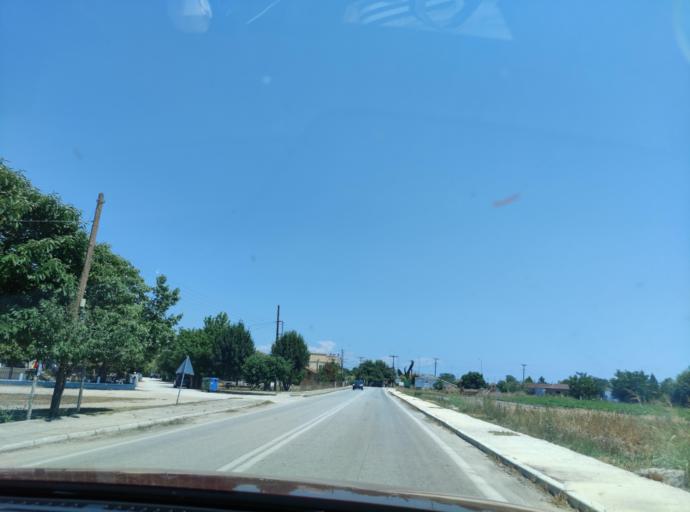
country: GR
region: East Macedonia and Thrace
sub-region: Nomos Kavalas
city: Nea Karya
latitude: 40.9041
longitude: 24.6675
